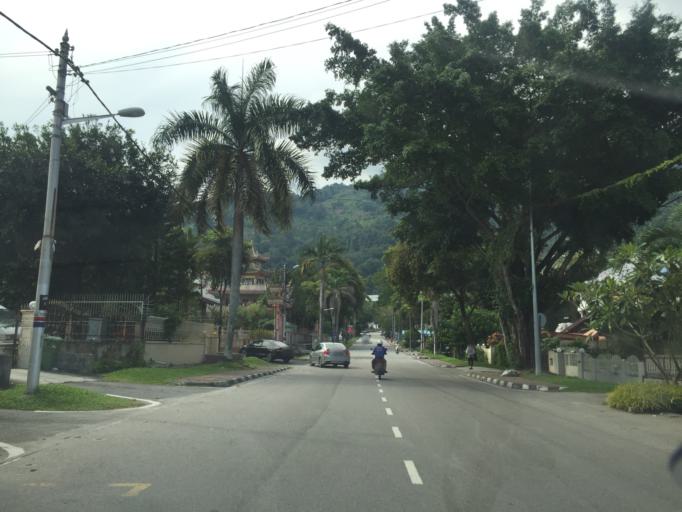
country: MY
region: Penang
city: George Town
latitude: 5.4062
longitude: 100.2816
